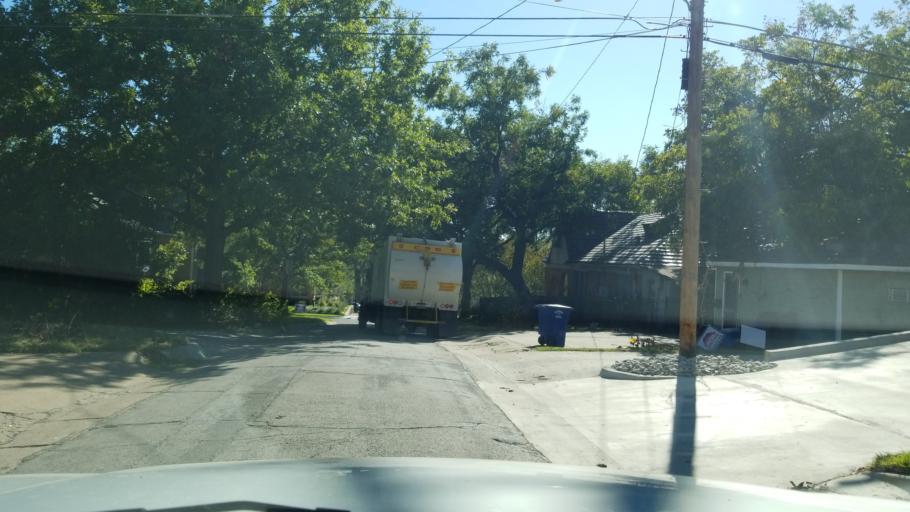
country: US
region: Texas
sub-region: Dallas County
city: Highland Park
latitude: 32.8029
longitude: -96.7410
